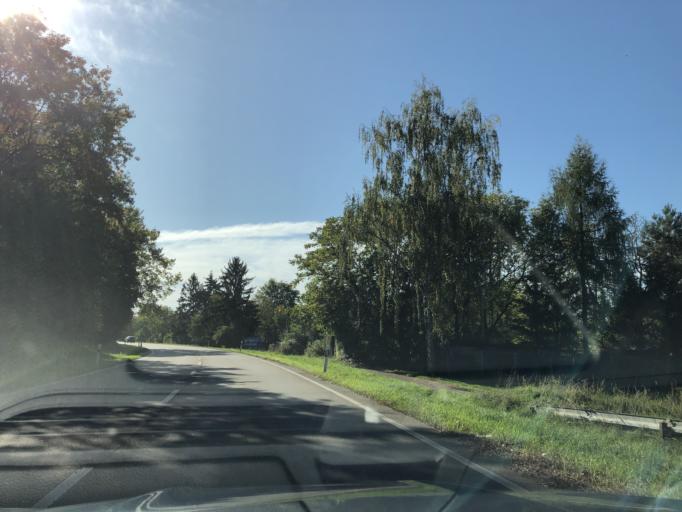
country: DE
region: Baden-Wuerttemberg
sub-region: Karlsruhe Region
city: Eppelheim
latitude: 49.3794
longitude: 8.6562
